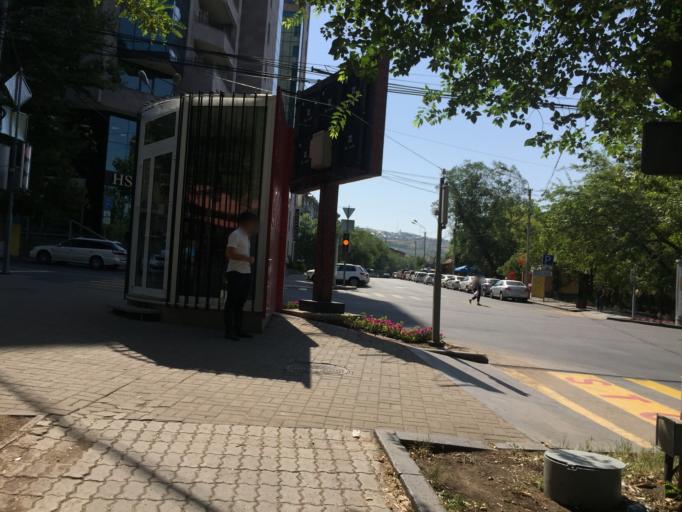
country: AM
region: Yerevan
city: Yerevan
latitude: 40.1881
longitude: 44.5204
